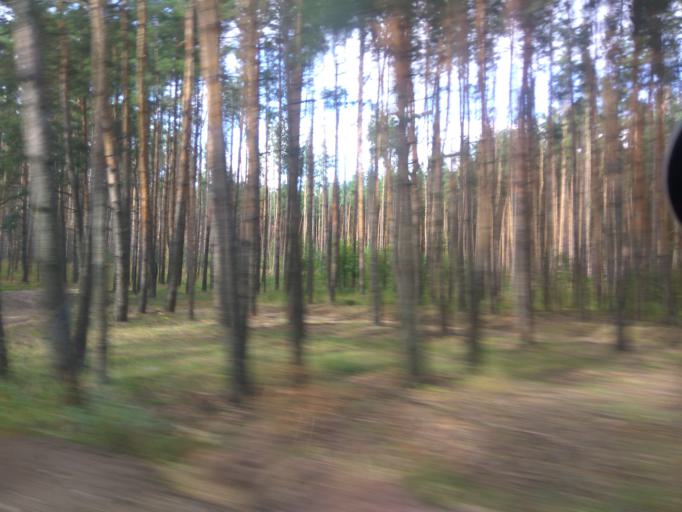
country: RU
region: Moskovskaya
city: Bronnitsy
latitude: 55.4704
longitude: 38.2749
